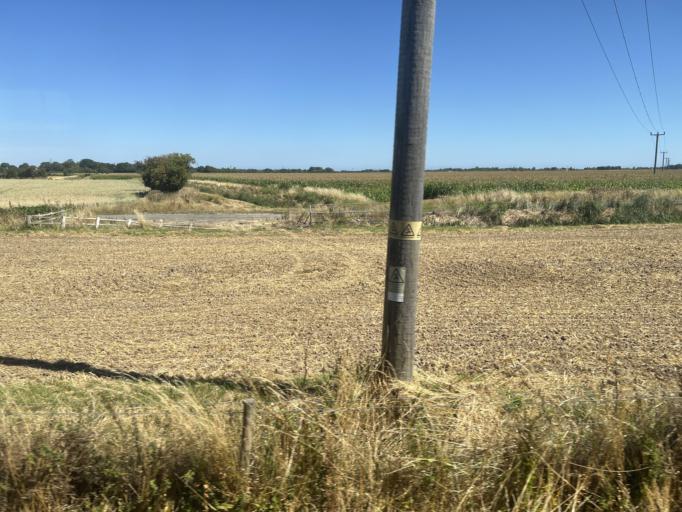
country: GB
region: England
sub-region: Lincolnshire
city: Wainfleet All Saints
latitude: 53.1148
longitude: 0.2139
